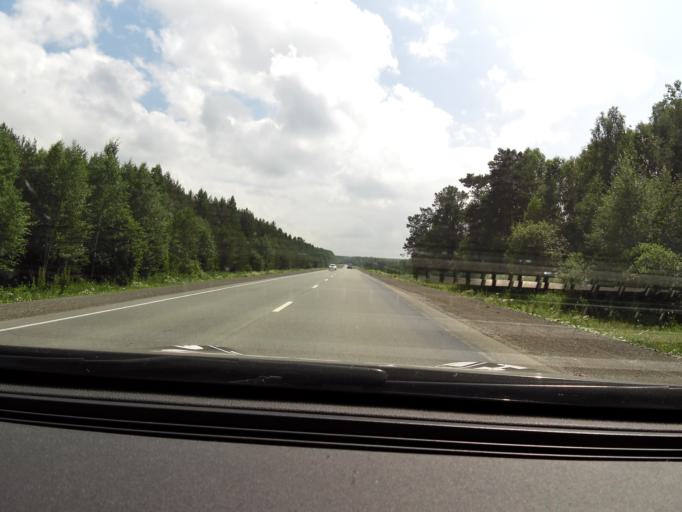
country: RU
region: Perm
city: Suksun
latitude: 57.0073
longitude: 57.4748
